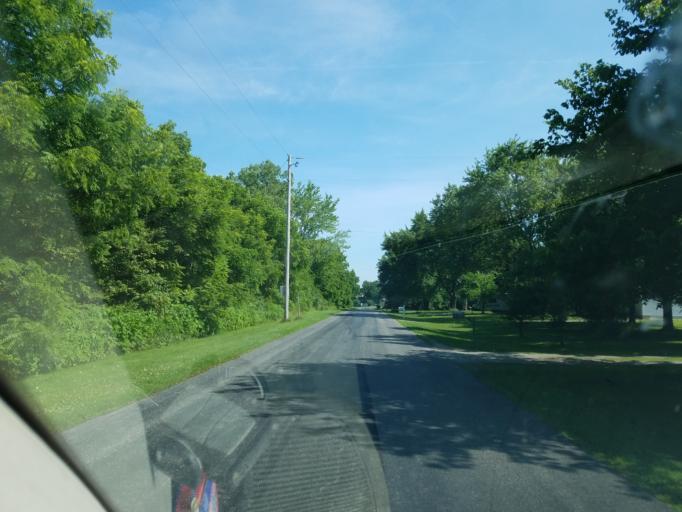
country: US
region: Ohio
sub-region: Marion County
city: Marion
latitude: 40.6490
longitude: -83.0913
